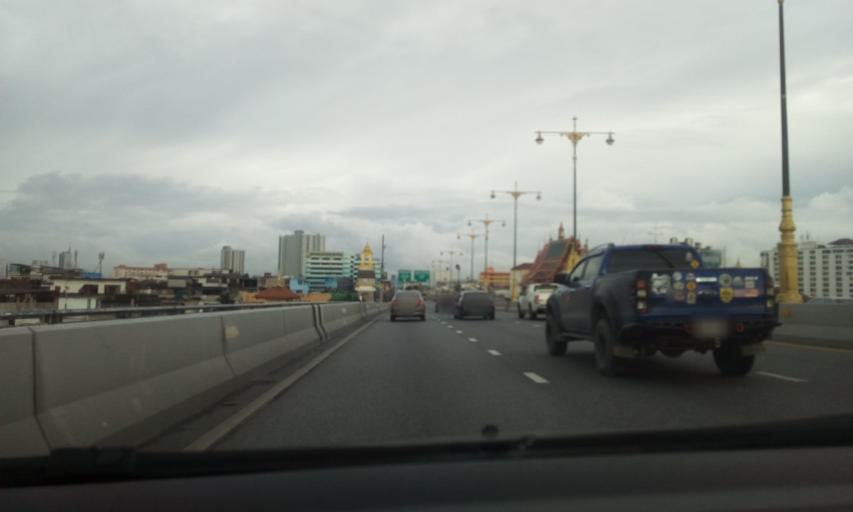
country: TH
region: Nonthaburi
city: Pak Kret
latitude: 13.9154
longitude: 100.4944
